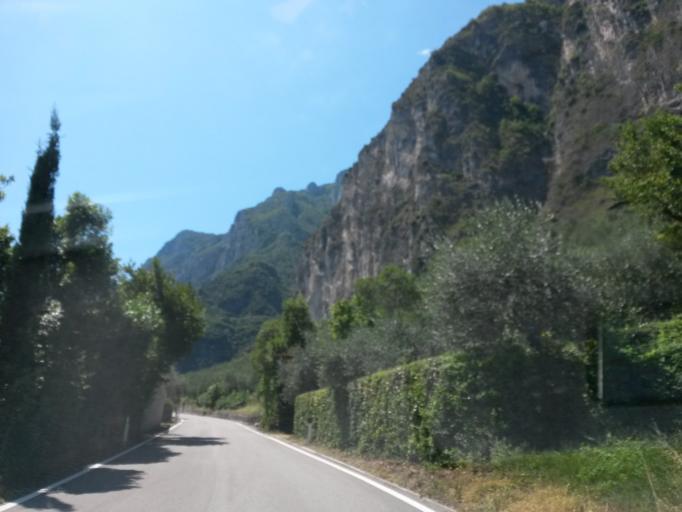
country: IT
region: Trentino-Alto Adige
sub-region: Provincia di Trento
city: Tenno
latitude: 45.9035
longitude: 10.8328
